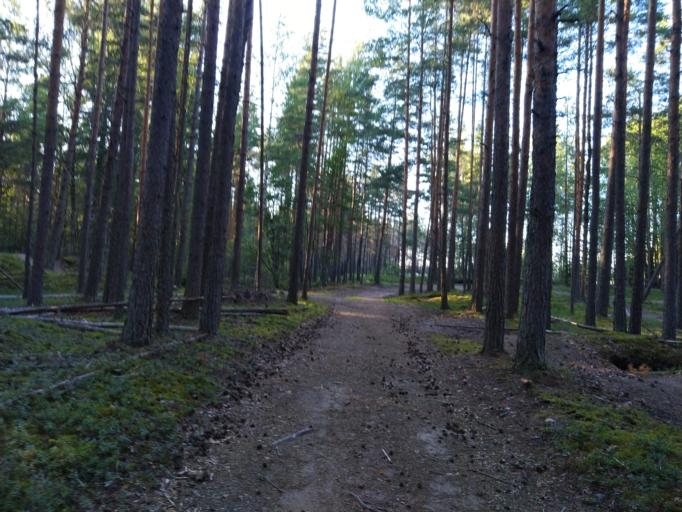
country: FI
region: Varsinais-Suomi
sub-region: Turku
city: Rusko
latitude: 60.5074
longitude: 22.2581
